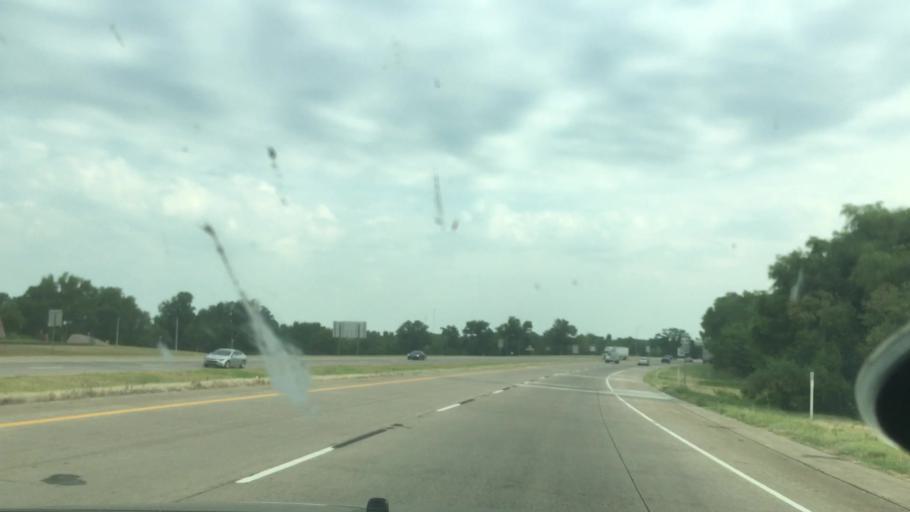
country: US
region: Oklahoma
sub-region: Bryan County
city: Colbert
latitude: 33.8174
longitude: -96.5350
